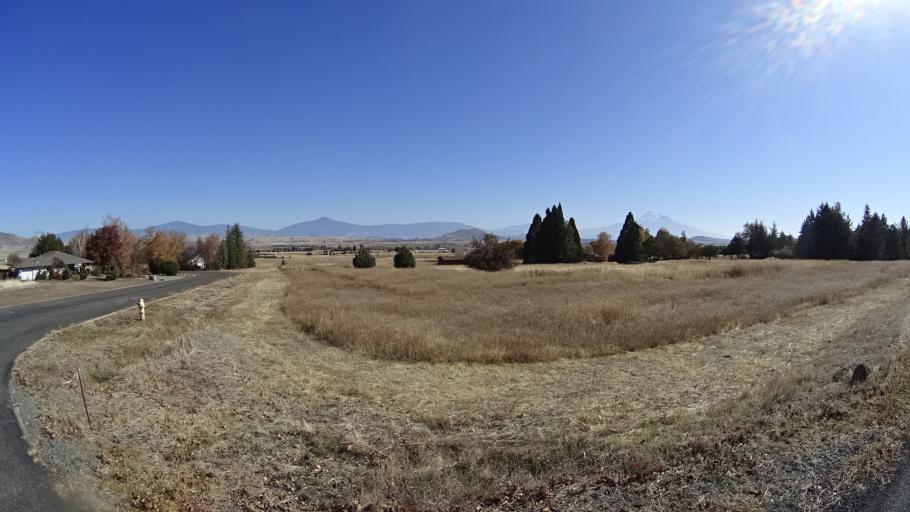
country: US
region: California
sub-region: Siskiyou County
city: Yreka
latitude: 41.7441
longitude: -122.6030
